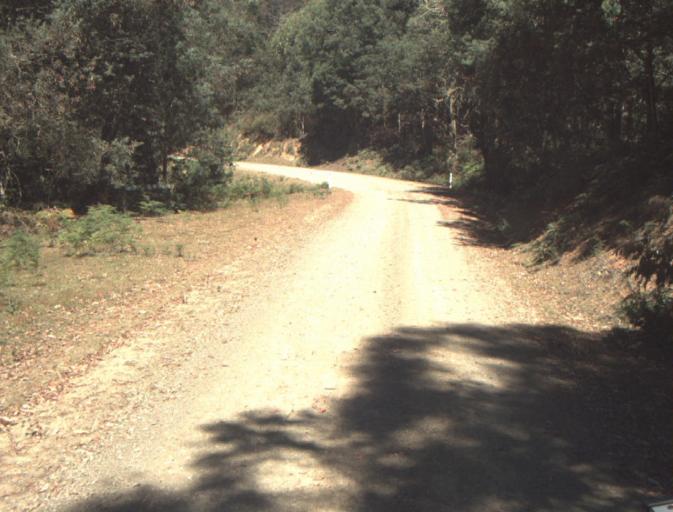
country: AU
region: Tasmania
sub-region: Dorset
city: Scottsdale
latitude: -41.3787
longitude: 147.4796
